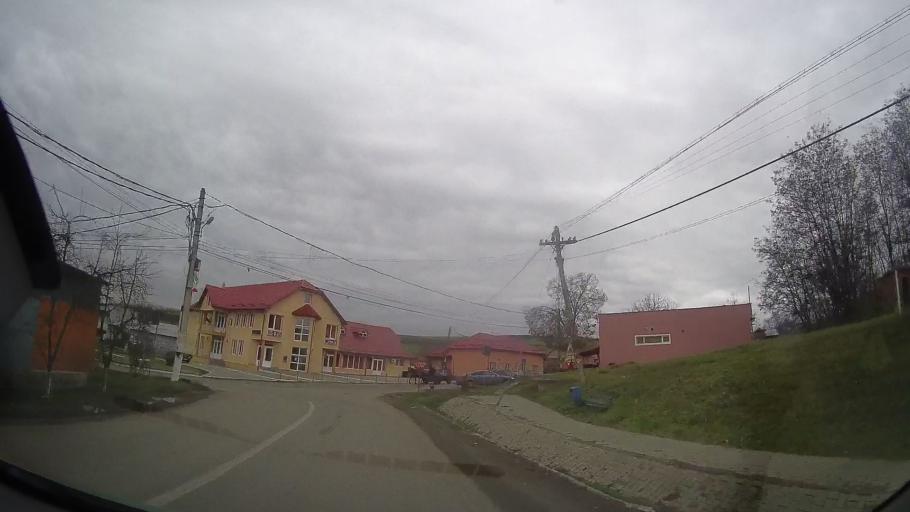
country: RO
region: Mures
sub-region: Comuna Craesti
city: Craiesti
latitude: 46.7558
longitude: 24.4213
